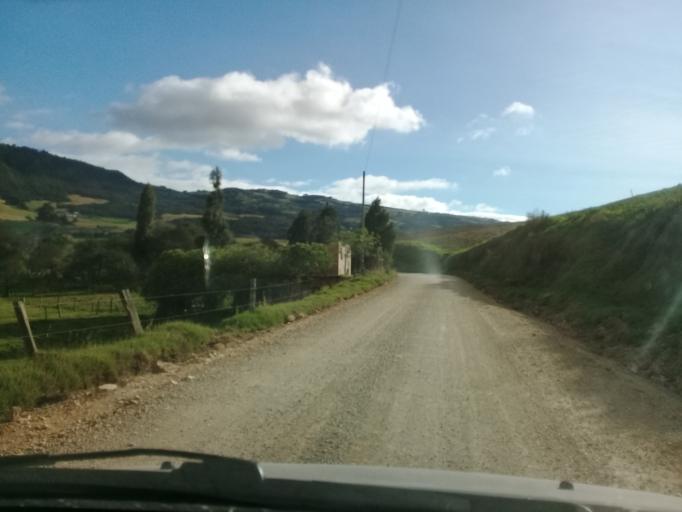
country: CO
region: Cundinamarca
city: Lenguazaque
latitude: 5.2738
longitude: -73.6559
